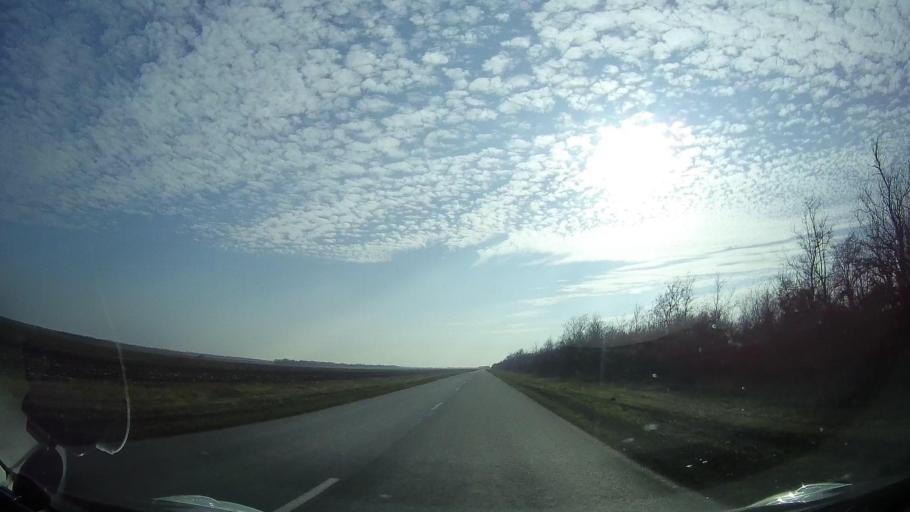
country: RU
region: Rostov
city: Veselyy
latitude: 46.9800
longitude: 40.7197
